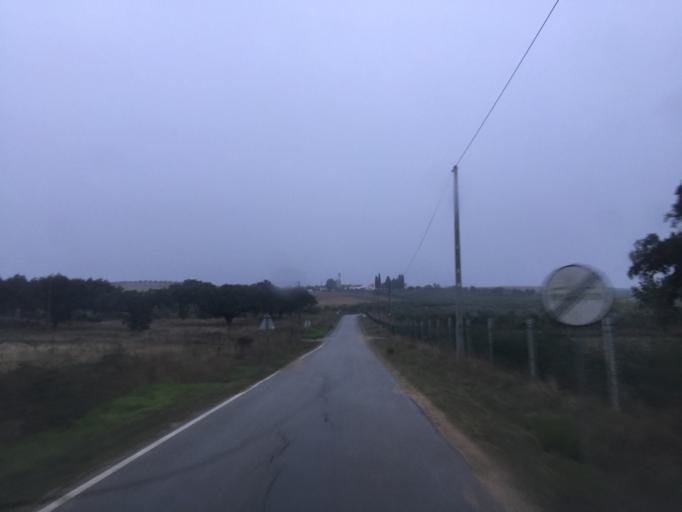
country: PT
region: Portalegre
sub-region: Avis
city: Avis
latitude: 39.0474
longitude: -7.9063
